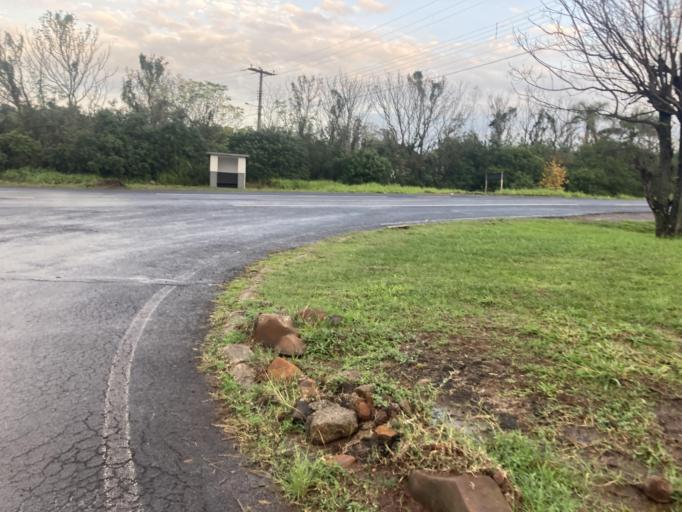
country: BR
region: Rio Grande do Sul
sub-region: Sao Pedro Do Butia
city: Butia Inferior
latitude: -27.9926
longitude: -54.8335
